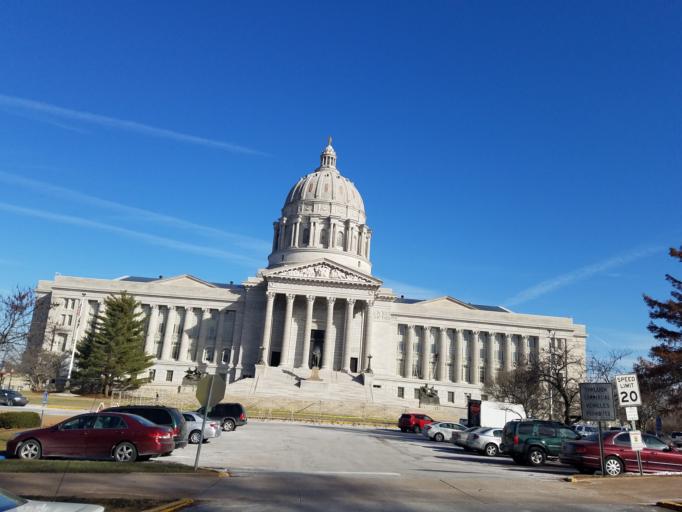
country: US
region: Missouri
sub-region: Cole County
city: Jefferson City
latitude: 38.5784
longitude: -92.1747
